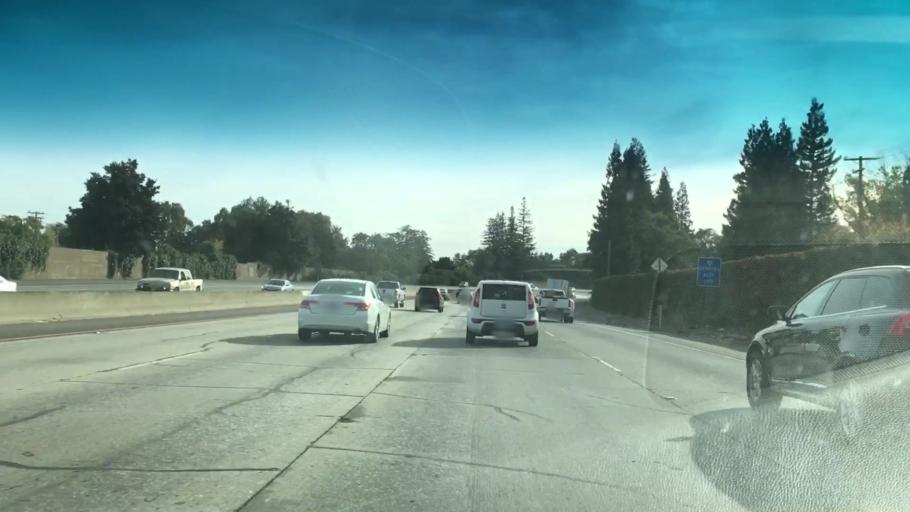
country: US
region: California
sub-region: Yolo County
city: West Sacramento
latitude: 38.5314
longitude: -121.5178
